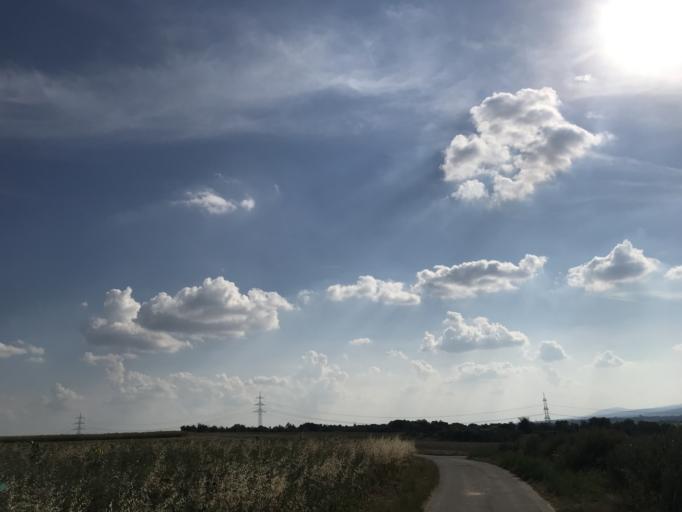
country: DE
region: Hesse
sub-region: Regierungsbezirk Darmstadt
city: Wolfersheim
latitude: 50.3517
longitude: 8.8144
